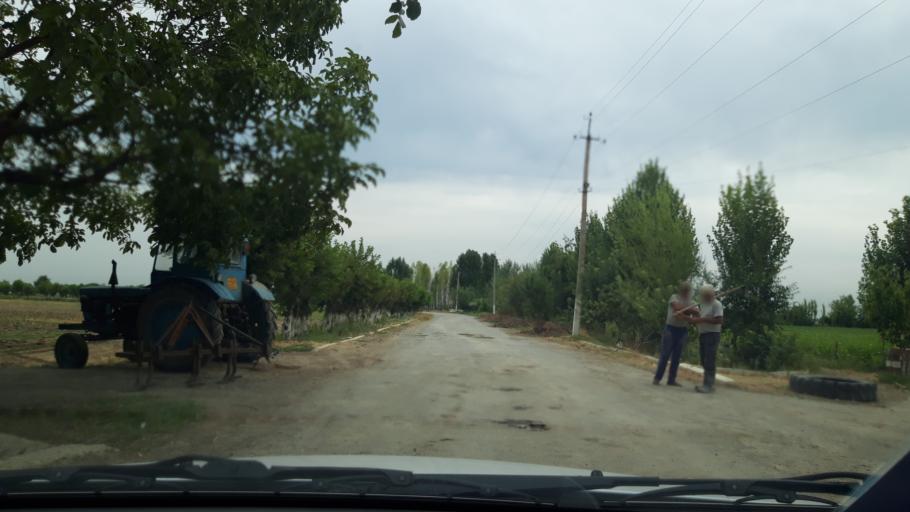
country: UZ
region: Namangan
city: Uychi
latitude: 41.0188
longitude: 71.9183
